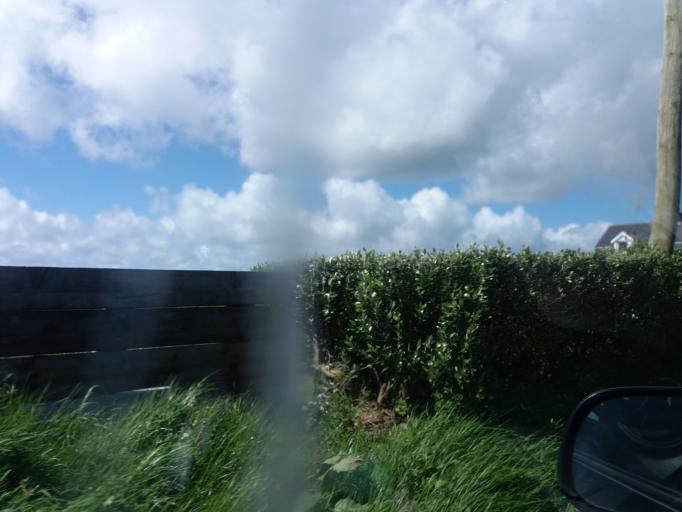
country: IE
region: Munster
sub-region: Waterford
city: Dunmore East
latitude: 52.1638
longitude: -6.8937
